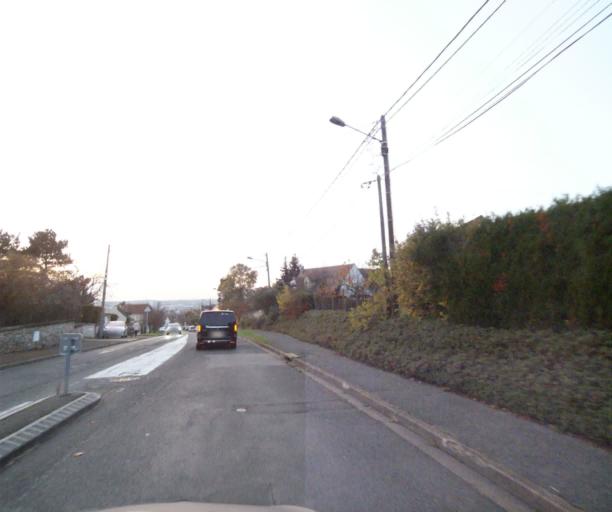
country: FR
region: Ile-de-France
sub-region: Departement des Yvelines
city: Triel-sur-Seine
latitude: 48.9756
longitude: 2.0148
